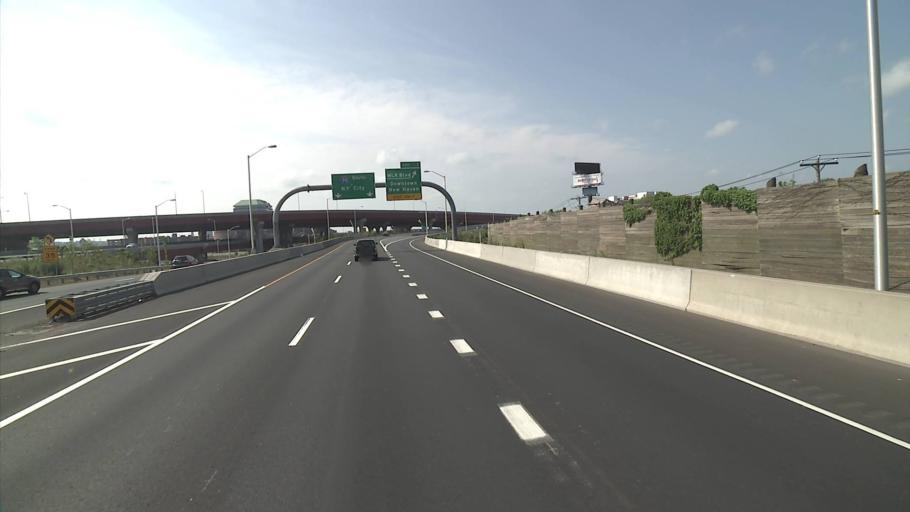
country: US
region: Connecticut
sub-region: New Haven County
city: New Haven
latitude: 41.3034
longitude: -72.9143
